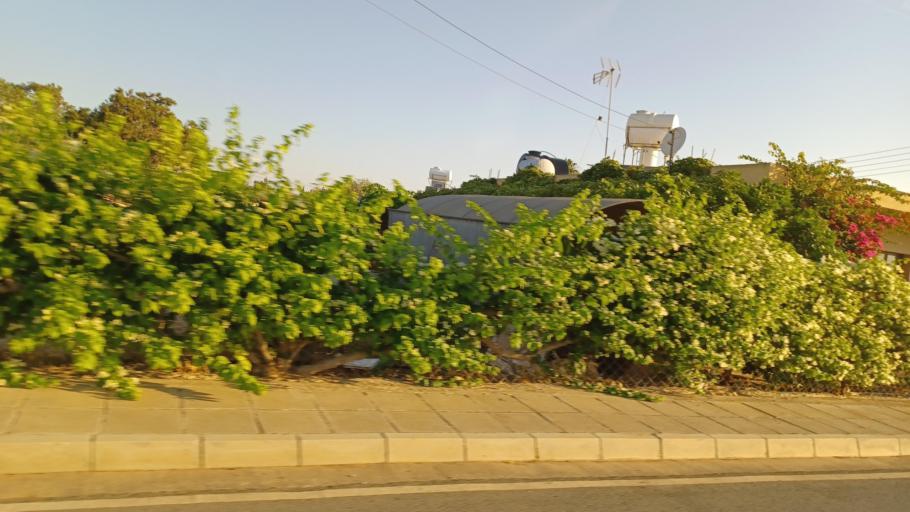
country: CY
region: Ammochostos
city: Achna
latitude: 35.0330
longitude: 33.7717
